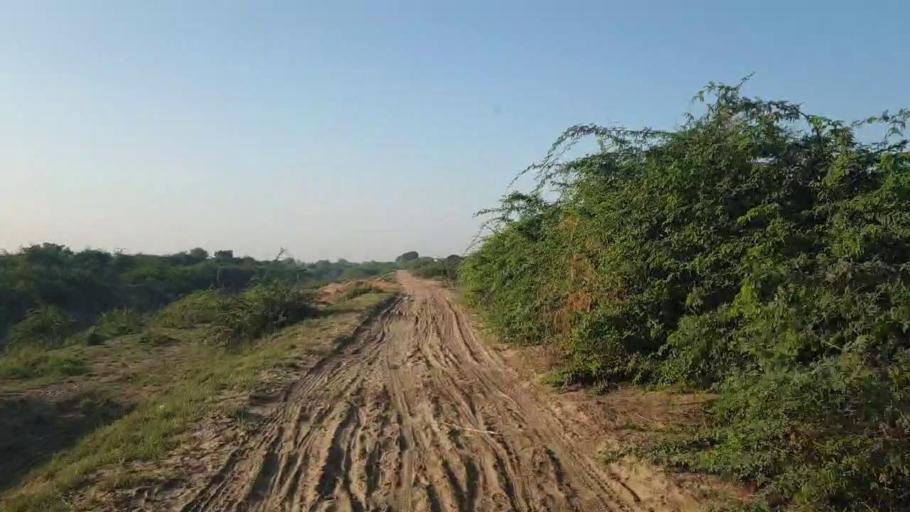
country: PK
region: Sindh
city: Badin
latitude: 24.6138
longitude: 68.7855
